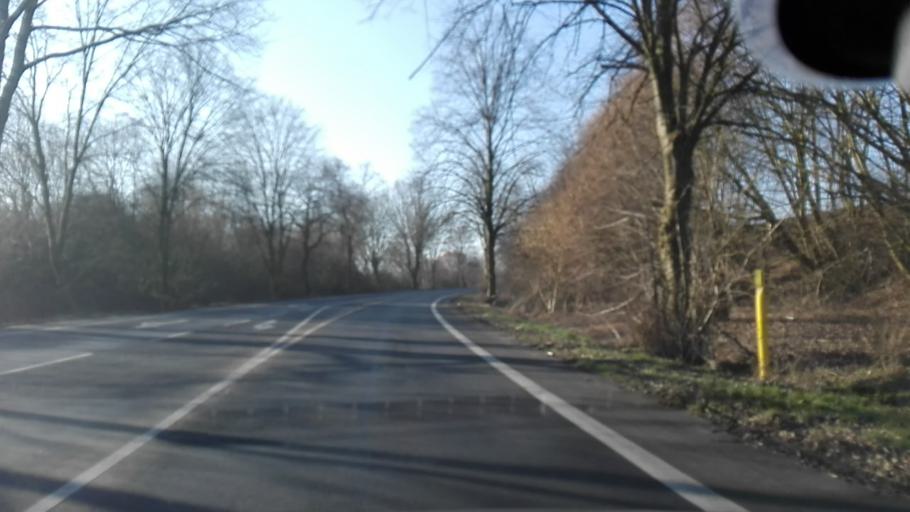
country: DE
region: North Rhine-Westphalia
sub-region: Regierungsbezirk Arnsberg
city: Unna
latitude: 51.5239
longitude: 7.6704
